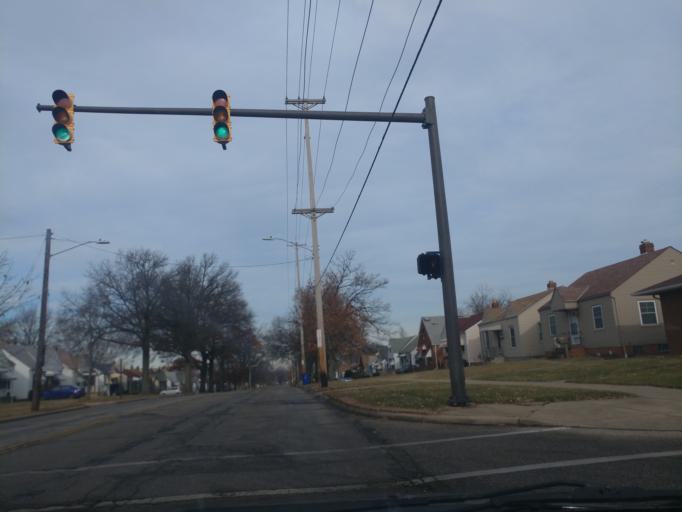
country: US
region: Ohio
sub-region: Cuyahoga County
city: Brooklyn
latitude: 41.4339
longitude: -81.7233
